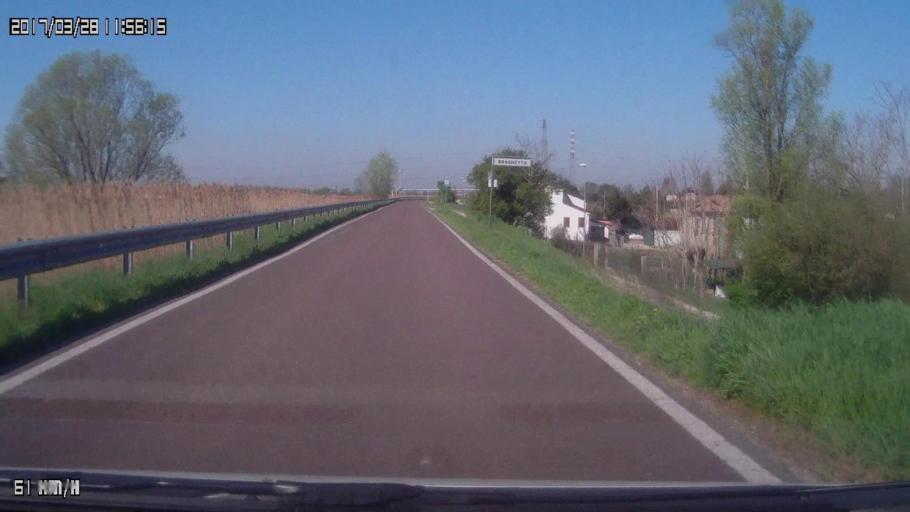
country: IT
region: Veneto
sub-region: Provincia di Venezia
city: Boscochiaro
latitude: 45.1327
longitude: 12.1405
